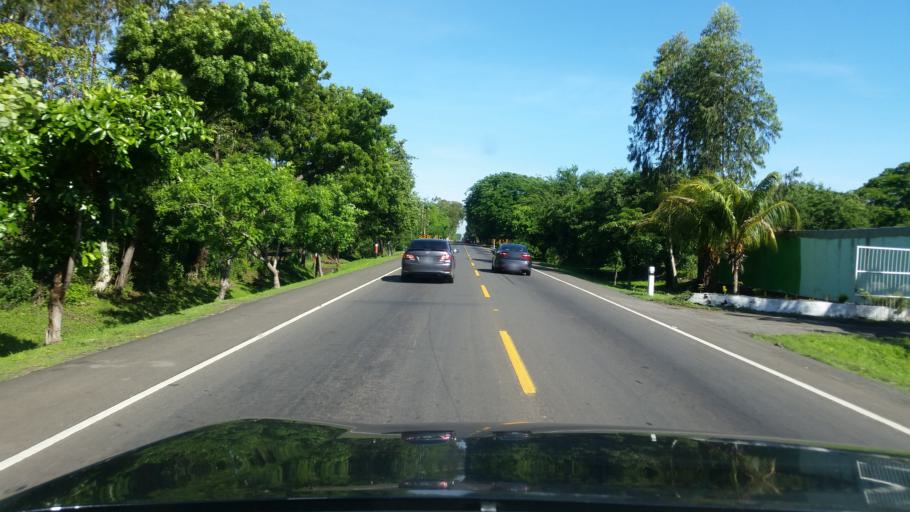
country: NI
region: Chinandega
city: Chichigalpa
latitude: 12.5873
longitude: -87.0145
